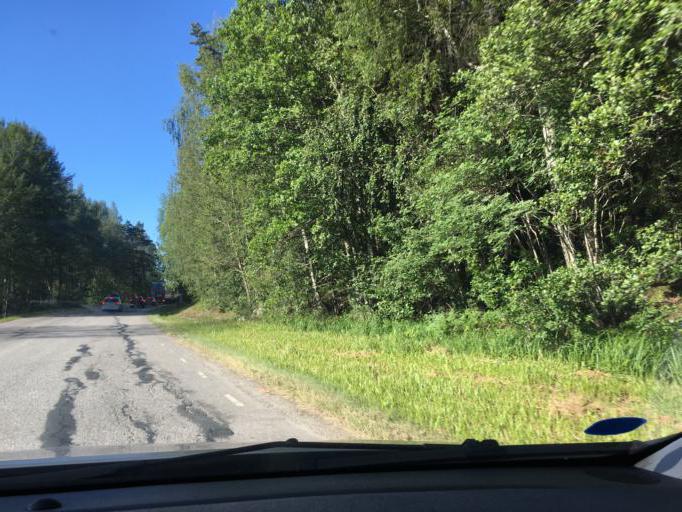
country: SE
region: Stockholm
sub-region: Sodertalje Kommun
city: Soedertaelje
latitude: 59.2100
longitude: 17.6520
